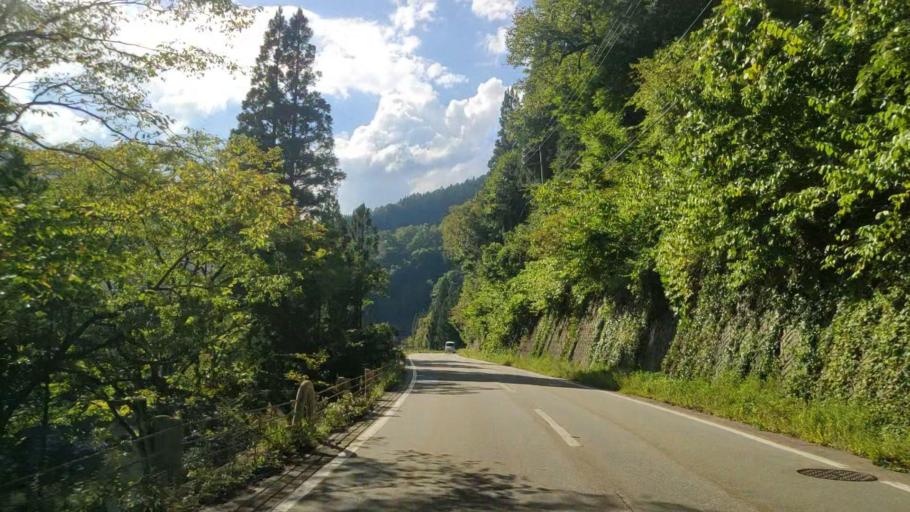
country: JP
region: Gifu
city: Takayama
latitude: 36.2974
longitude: 137.1270
